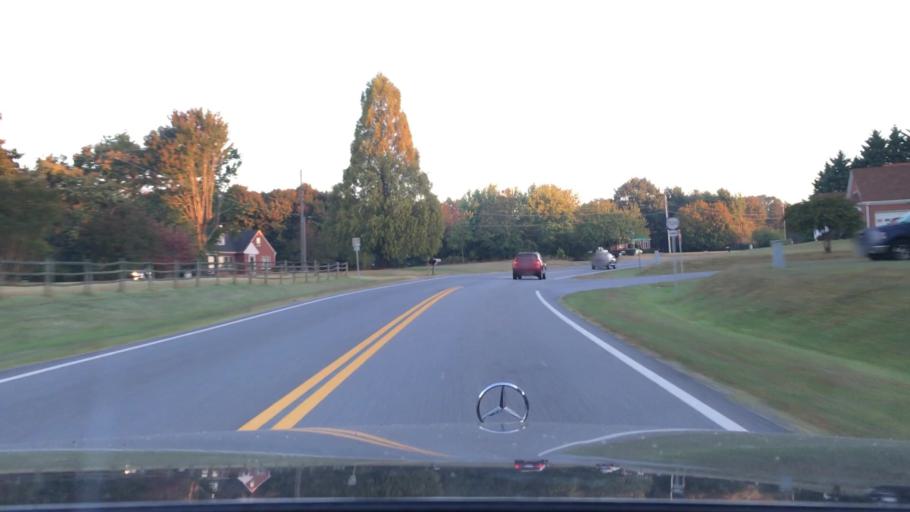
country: US
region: Virginia
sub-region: Campbell County
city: Timberlake
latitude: 37.3148
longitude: -79.2387
